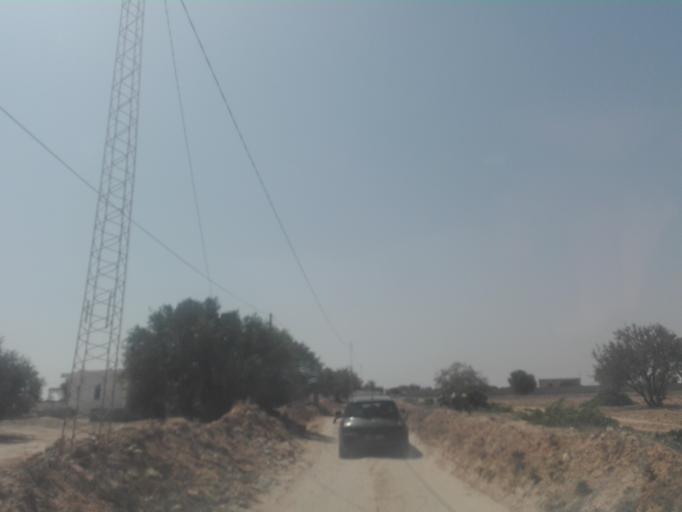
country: TN
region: Madanin
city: Zarzis
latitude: 33.5267
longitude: 11.0662
